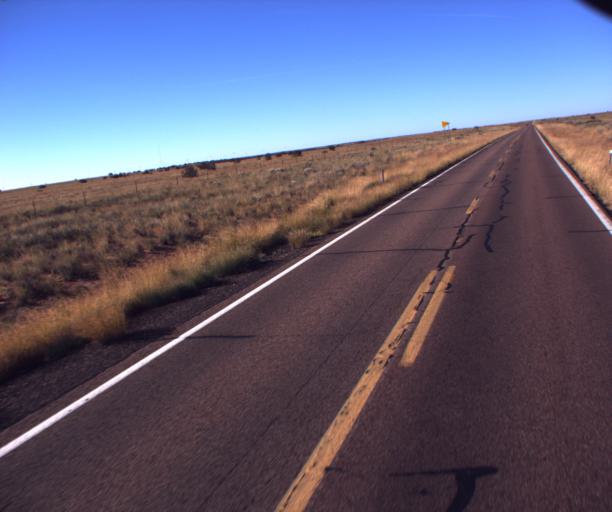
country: US
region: Arizona
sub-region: Navajo County
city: Holbrook
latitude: 34.7547
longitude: -110.2538
